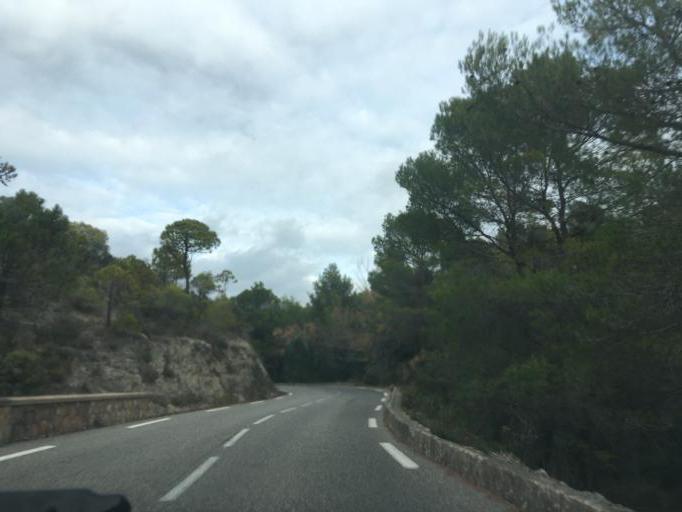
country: FR
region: Provence-Alpes-Cote d'Azur
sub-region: Departement du Var
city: Villecroze
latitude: 43.5858
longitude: 6.2693
